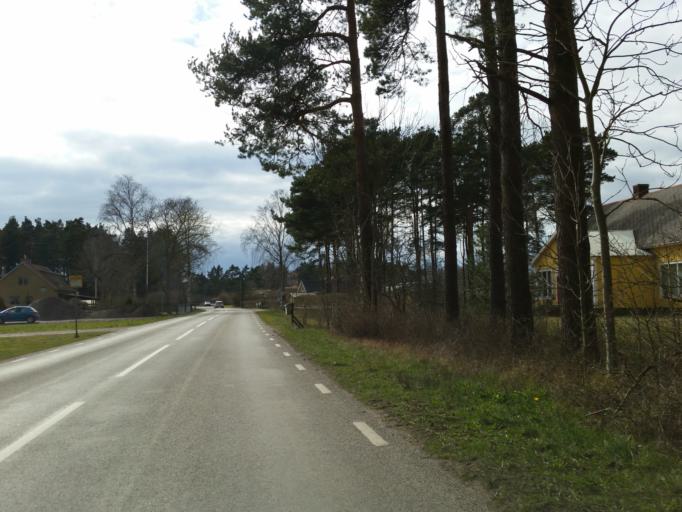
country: SE
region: Kalmar
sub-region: Morbylanga Kommun
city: Sodra Sandby
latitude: 56.6431
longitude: 16.6703
